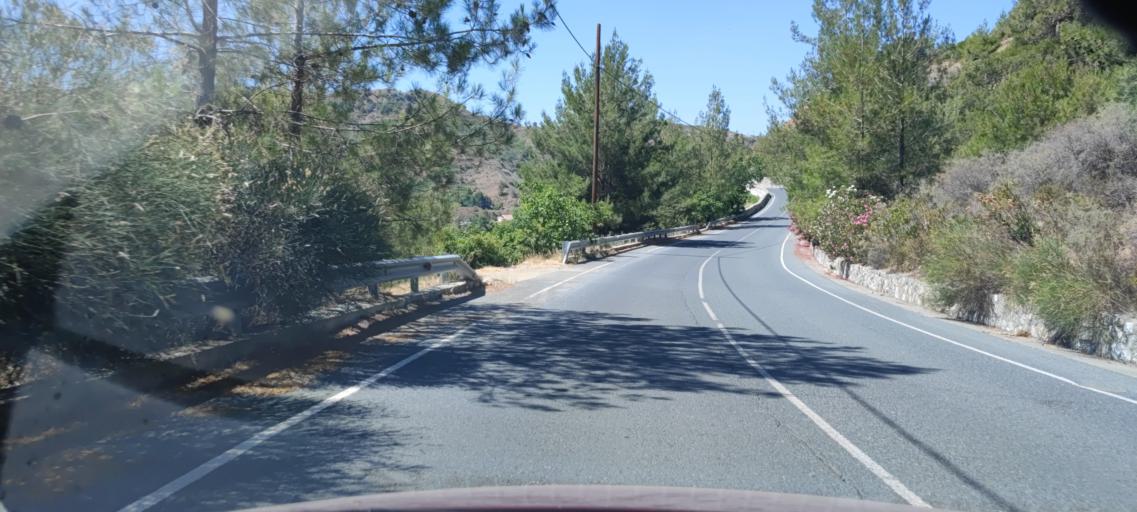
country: CY
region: Lefkosia
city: Kakopetria
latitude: 34.8965
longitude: 32.8360
